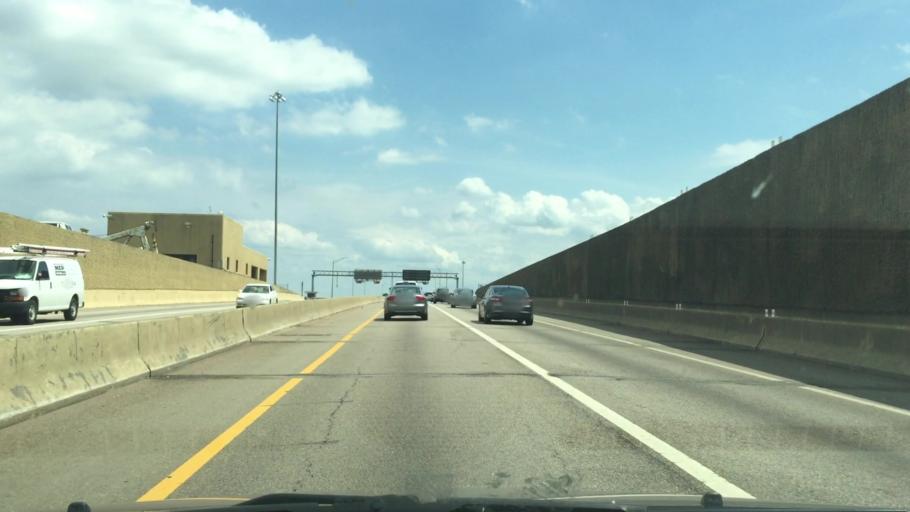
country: US
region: Virginia
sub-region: City of Newport News
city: Newport News
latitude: 36.9467
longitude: -76.4049
